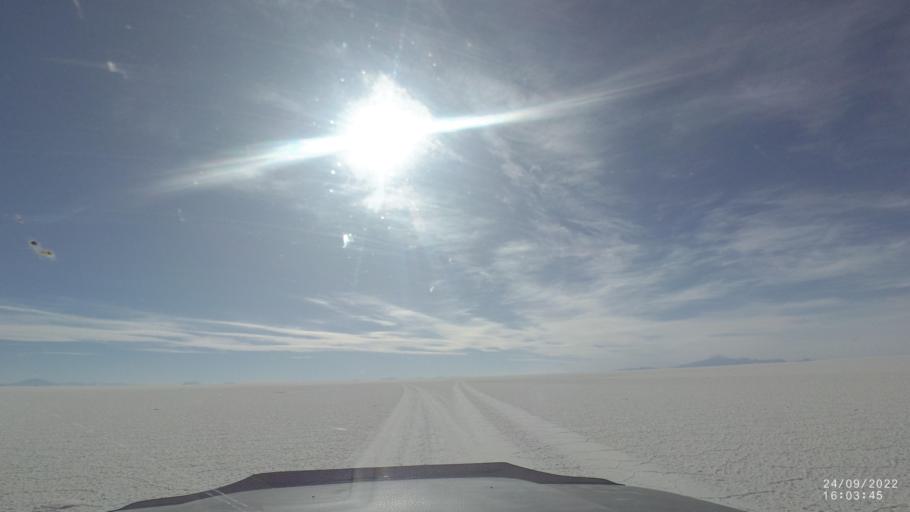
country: BO
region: Potosi
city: Colchani
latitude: -20.3125
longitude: -67.2857
